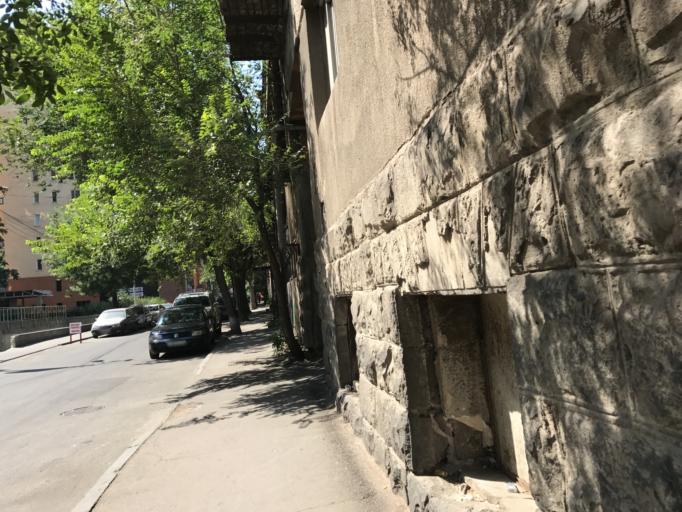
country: AM
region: Yerevan
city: Yerevan
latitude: 40.1799
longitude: 44.5166
